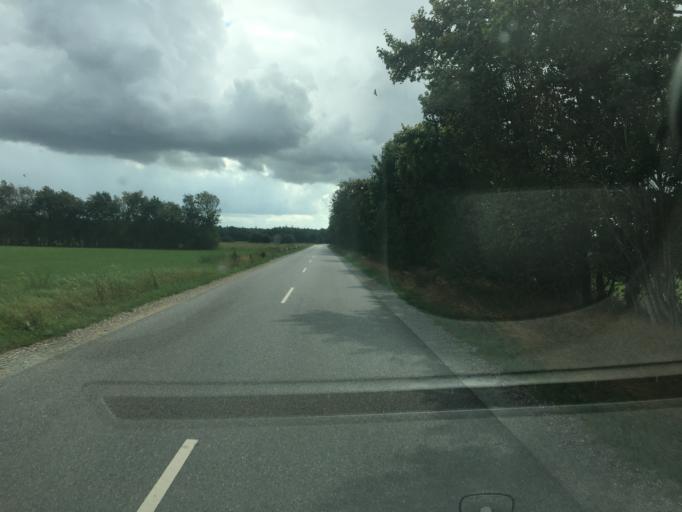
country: DK
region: South Denmark
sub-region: Tonder Kommune
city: Logumkloster
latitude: 55.0329
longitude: 8.9674
